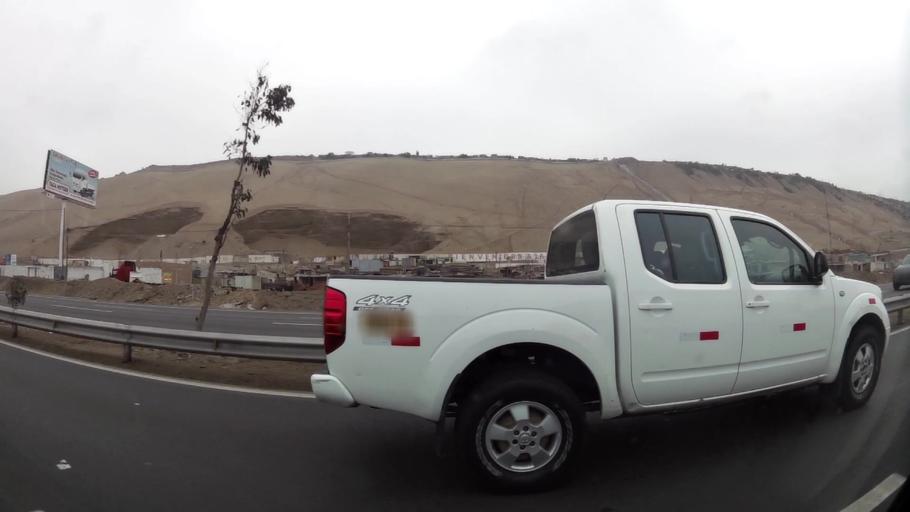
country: PE
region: Lima
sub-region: Lima
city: Surco
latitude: -12.2433
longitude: -76.9425
